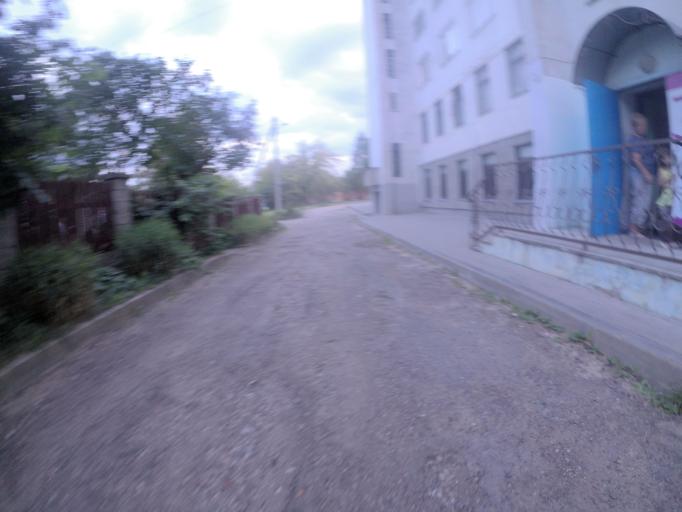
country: BY
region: Grodnenskaya
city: Hrodna
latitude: 53.6922
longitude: 23.8258
